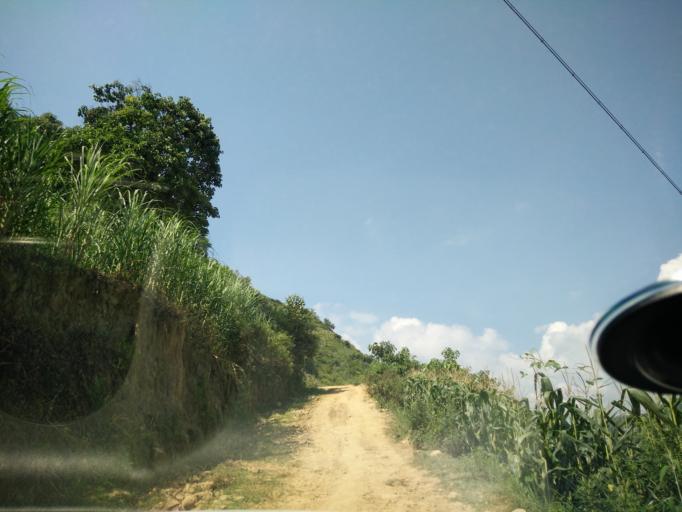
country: CN
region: Guangxi Zhuangzu Zizhiqu
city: Xinzhou
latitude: 25.1849
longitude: 105.6934
